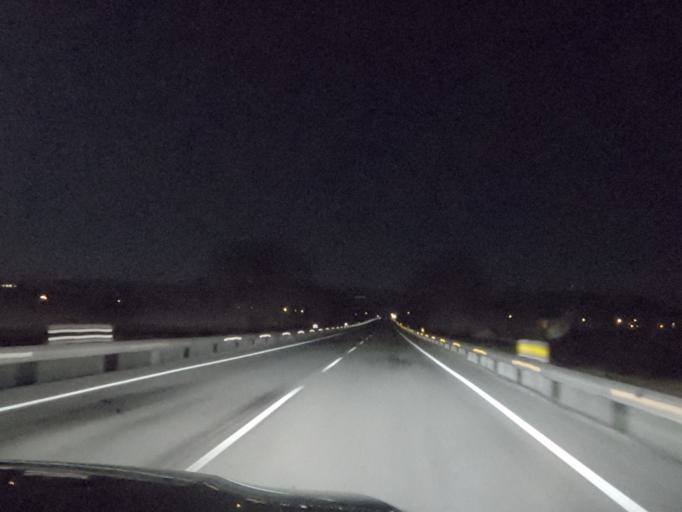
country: ES
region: Galicia
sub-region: Provincia de Ourense
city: Verin
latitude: 41.9521
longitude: -7.4958
